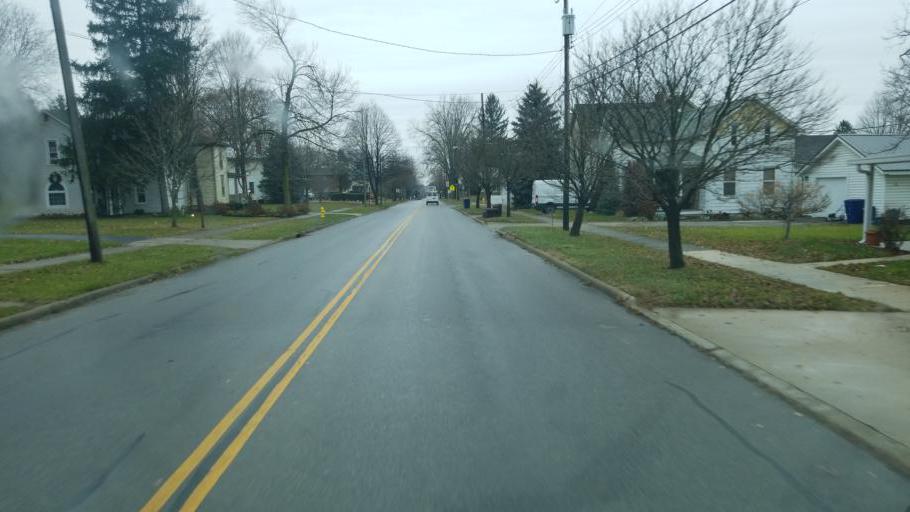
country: US
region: Ohio
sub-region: Delaware County
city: Delaware
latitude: 40.2980
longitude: -83.0509
